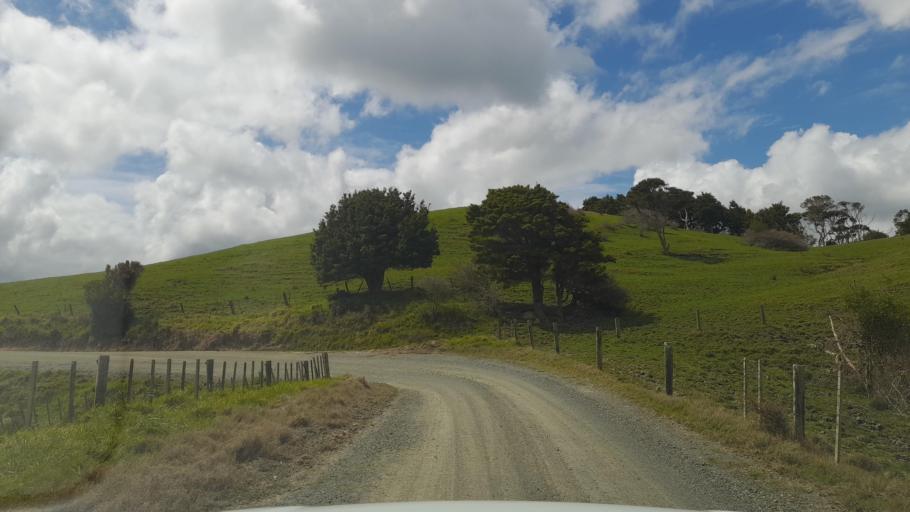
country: NZ
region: Auckland
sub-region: Auckland
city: Wellsford
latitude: -36.2130
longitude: 174.3256
